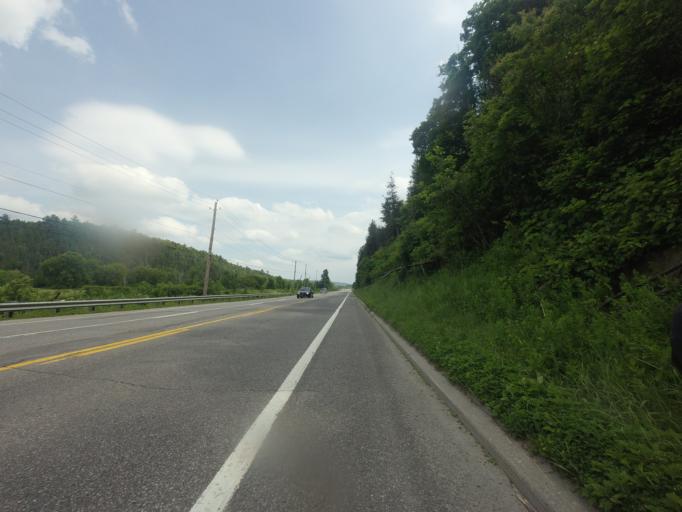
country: CA
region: Quebec
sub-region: Outaouais
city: Wakefield
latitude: 45.7565
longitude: -75.9183
